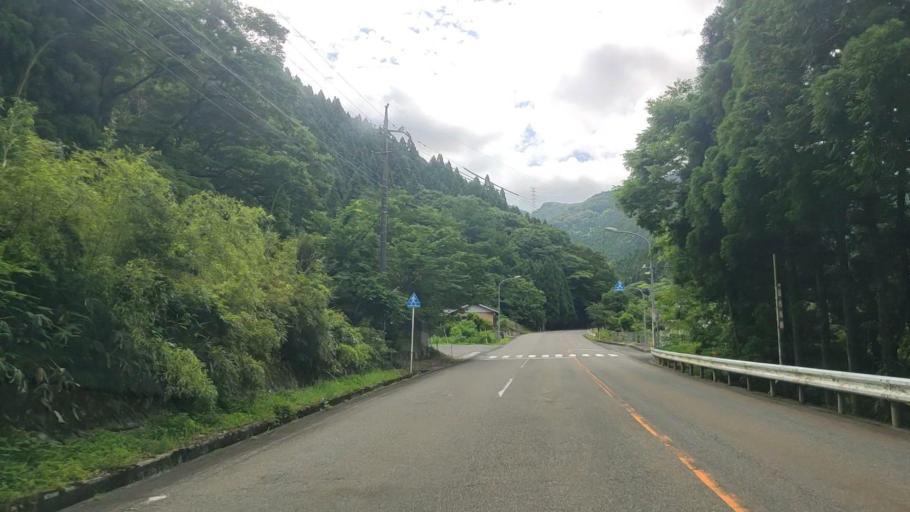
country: JP
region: Okayama
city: Niimi
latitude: 35.2077
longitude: 133.4931
